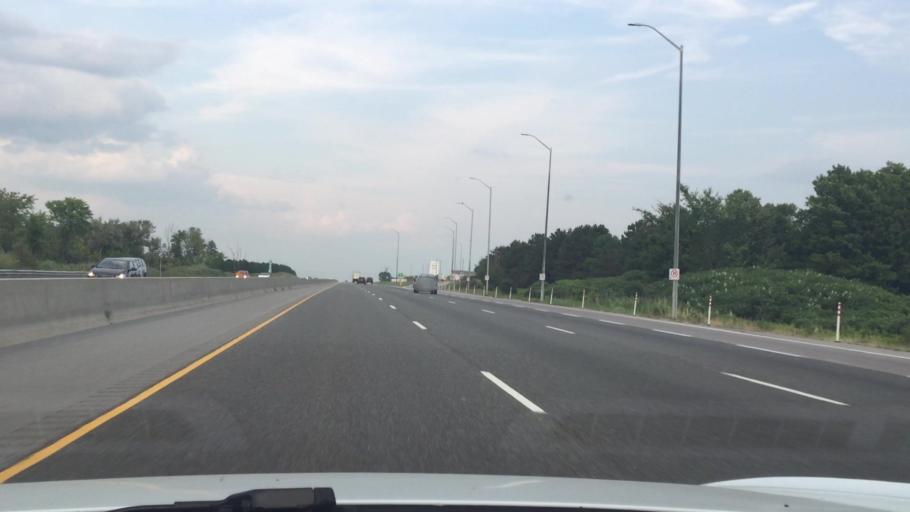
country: CA
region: Ontario
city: Cobourg
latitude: 43.9425
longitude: -78.4377
